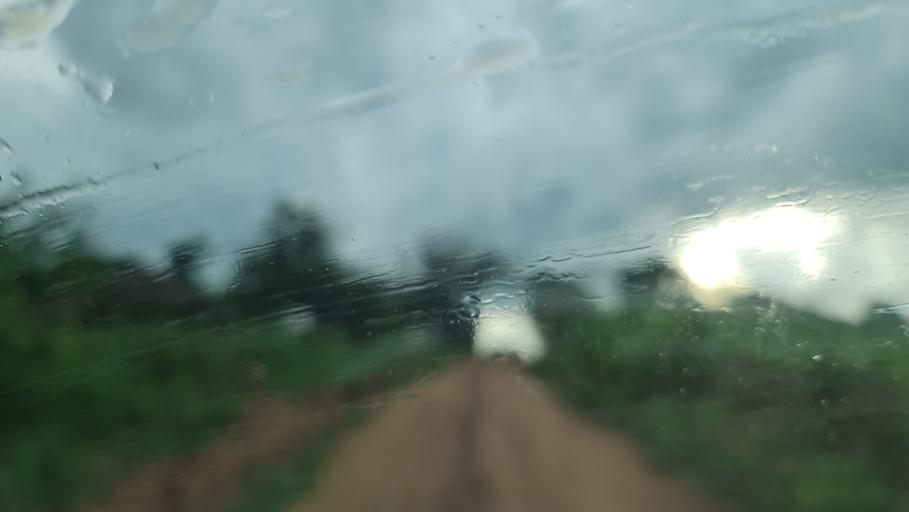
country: MZ
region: Nampula
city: Nacala
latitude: -13.9859
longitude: 40.3876
